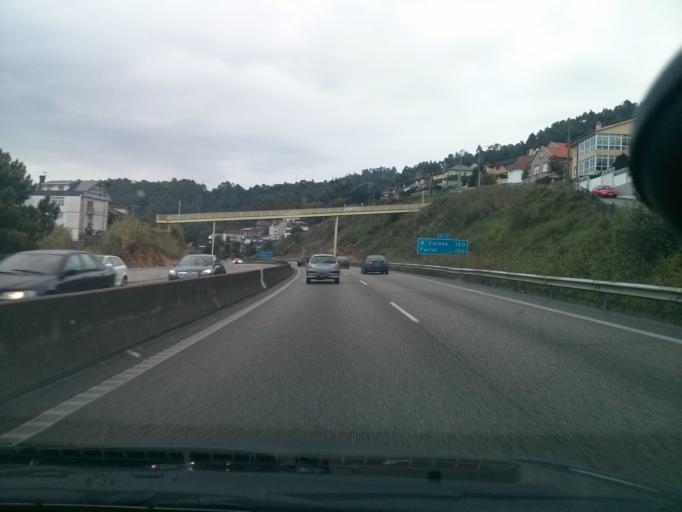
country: ES
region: Galicia
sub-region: Provincia de Pontevedra
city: Redondela
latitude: 42.2659
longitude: -8.6667
